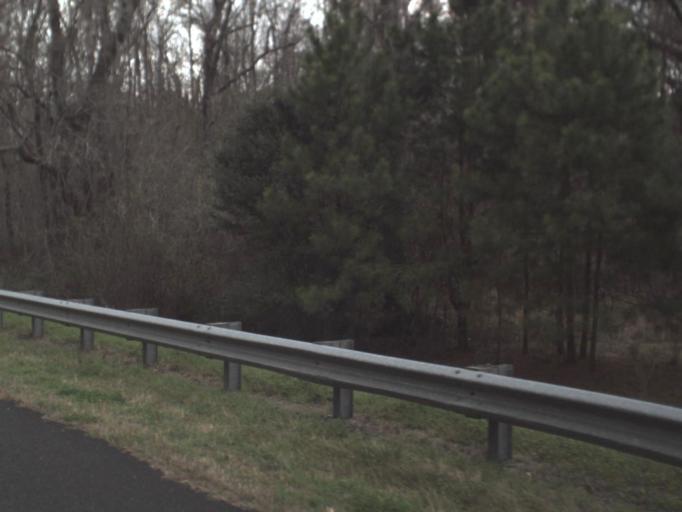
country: US
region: Georgia
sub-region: Grady County
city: Cairo
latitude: 30.6494
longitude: -84.1684
